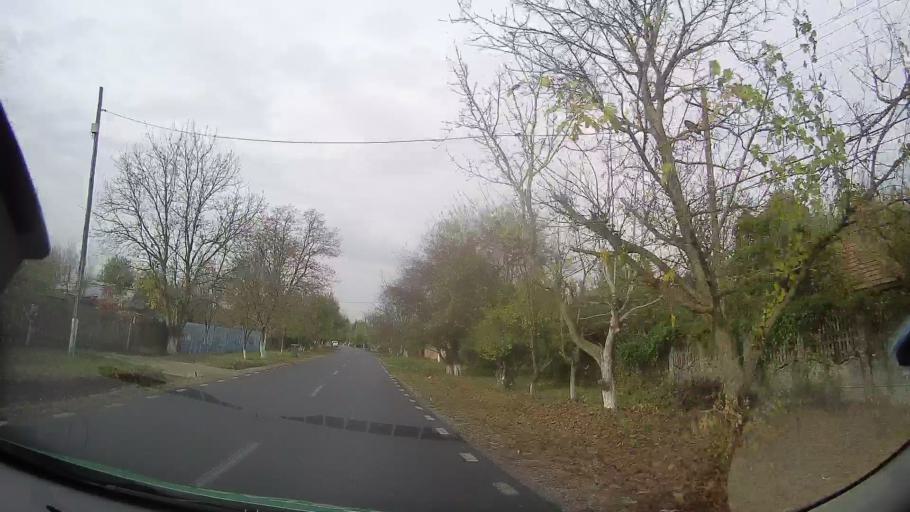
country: RO
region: Ilfov
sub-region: Comuna Nuci
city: Nuci
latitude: 44.7061
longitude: 26.3239
